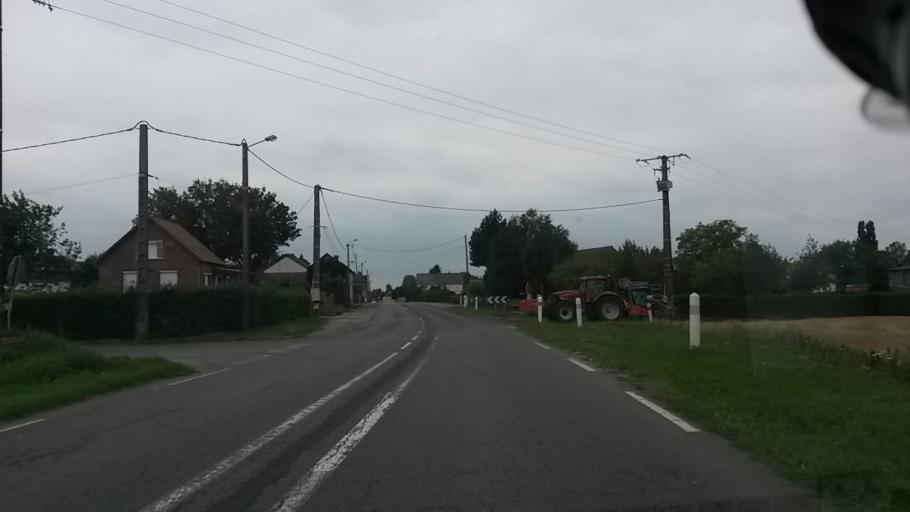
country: FR
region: Picardie
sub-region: Departement de la Somme
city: Hornoy-le-Bourg
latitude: 49.7805
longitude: 1.8956
